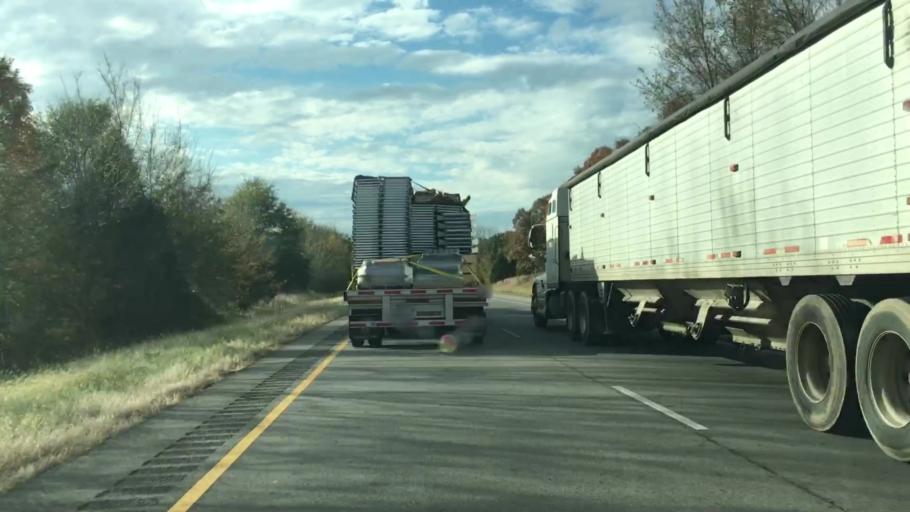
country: US
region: Arkansas
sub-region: Pope County
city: Pottsville
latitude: 35.2467
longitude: -93.0026
